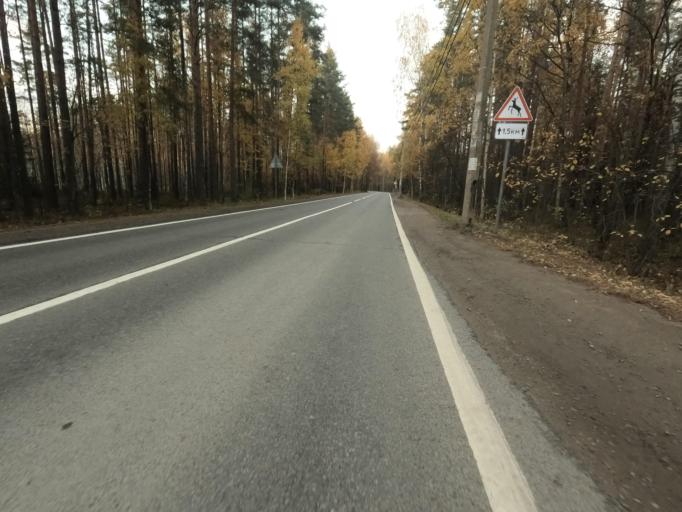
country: RU
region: St.-Petersburg
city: Repino
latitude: 60.1853
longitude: 29.8616
